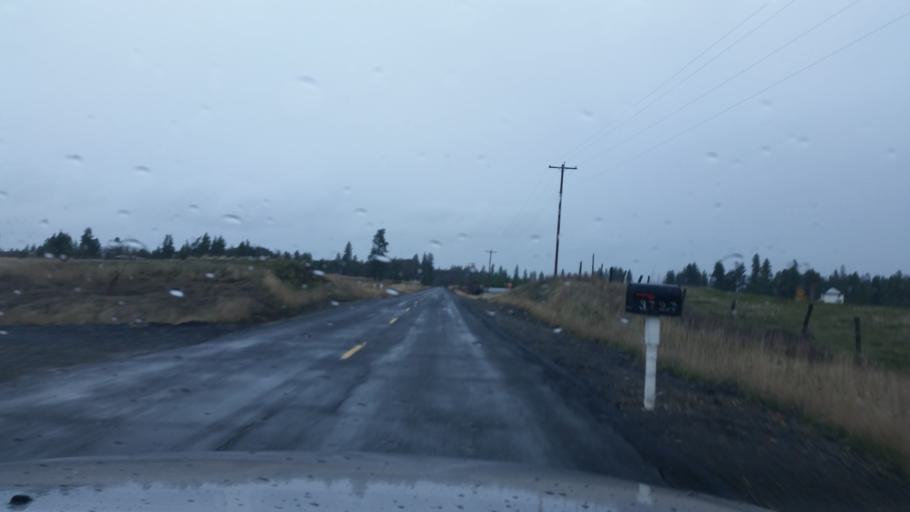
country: US
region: Washington
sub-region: Spokane County
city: Airway Heights
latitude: 47.6909
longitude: -117.5718
